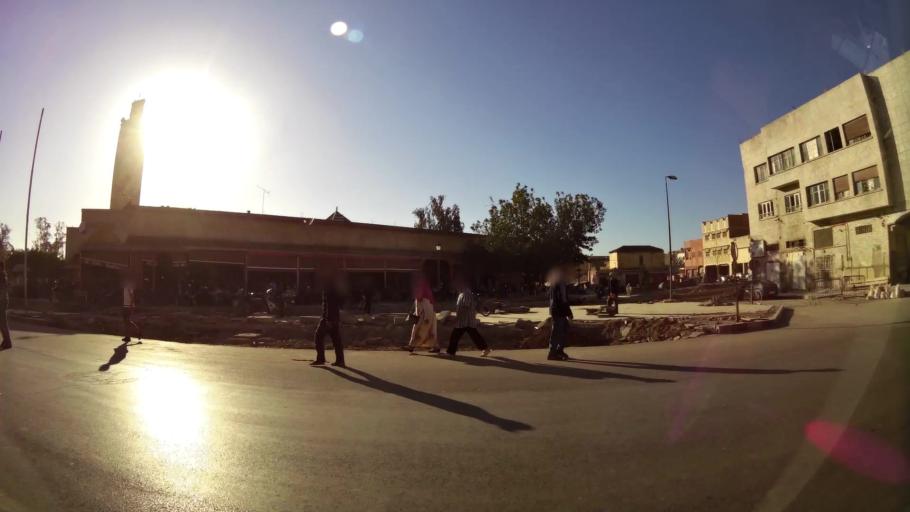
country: MA
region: Oriental
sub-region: Berkane-Taourirt
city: Berkane
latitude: 34.9231
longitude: -2.3366
